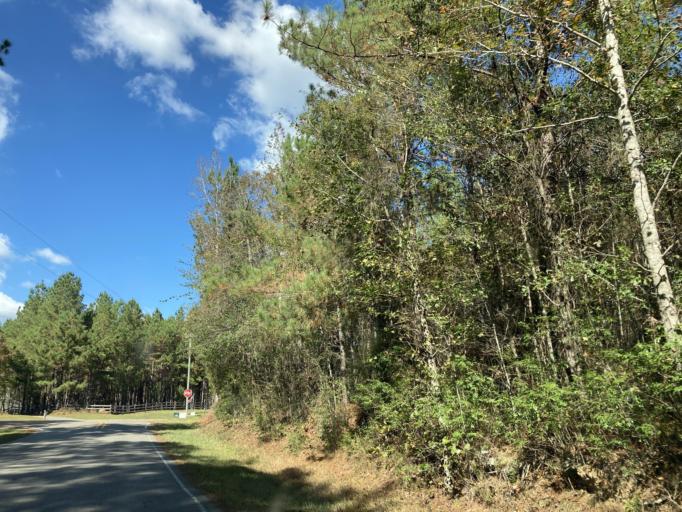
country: US
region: Mississippi
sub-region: Lamar County
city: Sumrall
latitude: 31.3512
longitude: -89.5536
